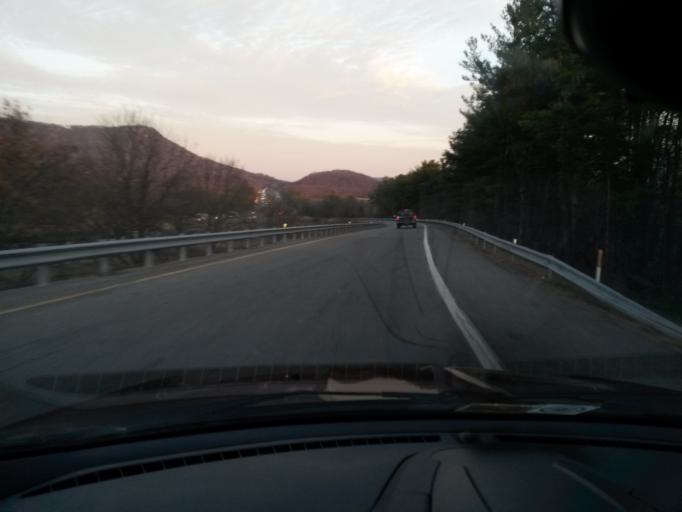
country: US
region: Virginia
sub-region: Roanoke County
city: Hollins
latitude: 37.3605
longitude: -79.9572
